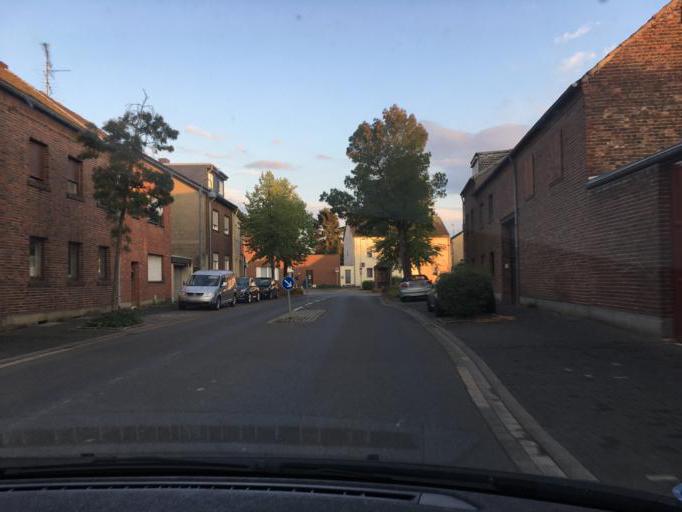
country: DE
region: North Rhine-Westphalia
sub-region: Regierungsbezirk Koln
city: Niederzier
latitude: 50.8533
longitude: 6.4590
